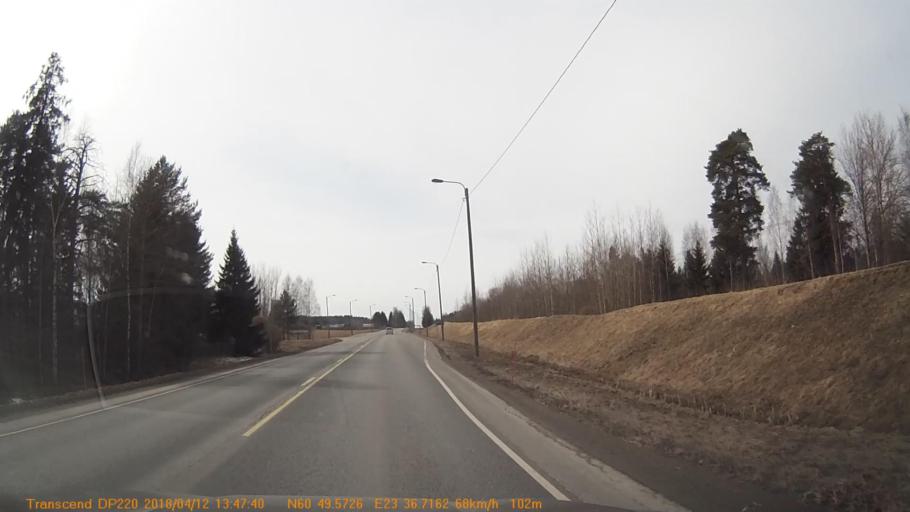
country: FI
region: Haeme
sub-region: Forssa
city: Forssa
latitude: 60.8262
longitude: 23.6117
